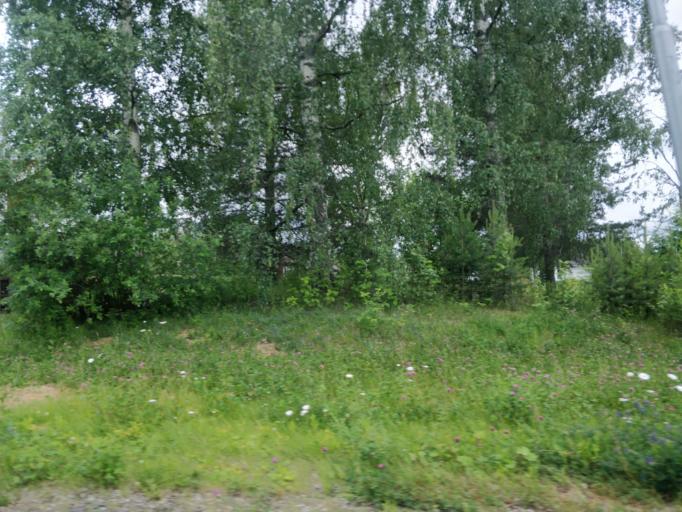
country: SE
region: Vaesterbotten
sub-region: Skelleftea Kommun
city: Viken
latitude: 64.7577
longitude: 20.8944
